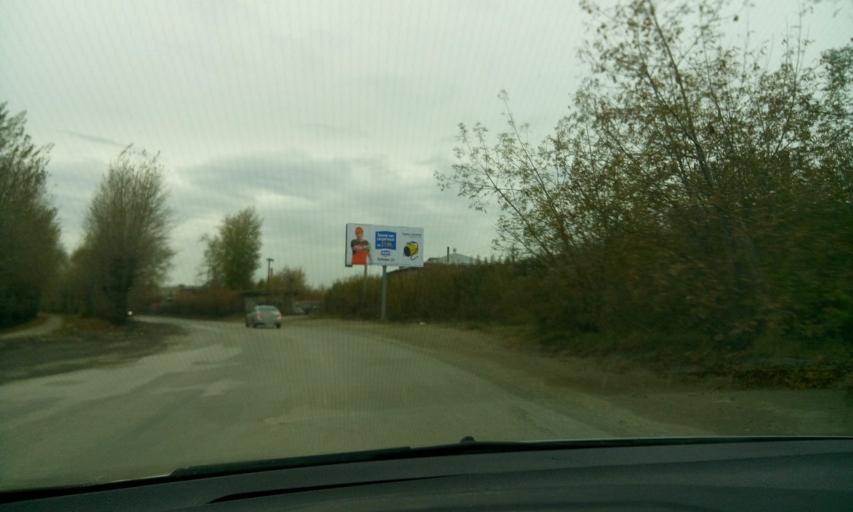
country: RU
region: Sverdlovsk
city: Yekaterinburg
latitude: 56.8768
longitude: 60.6234
